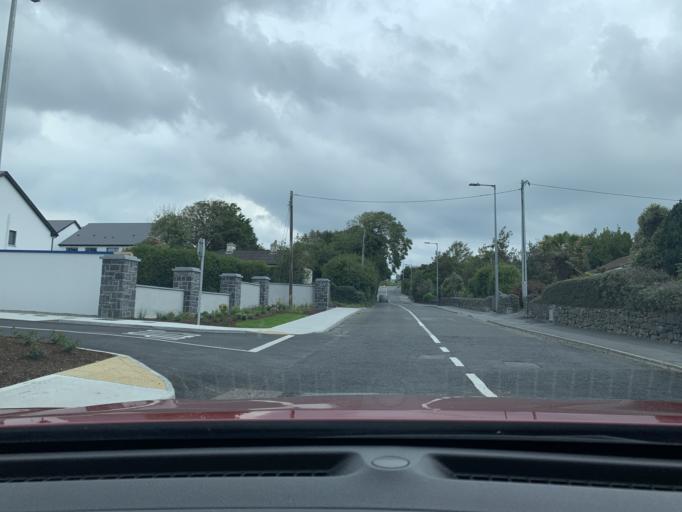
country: IE
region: Connaught
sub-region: County Galway
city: Bearna
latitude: 53.2657
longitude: -9.1173
